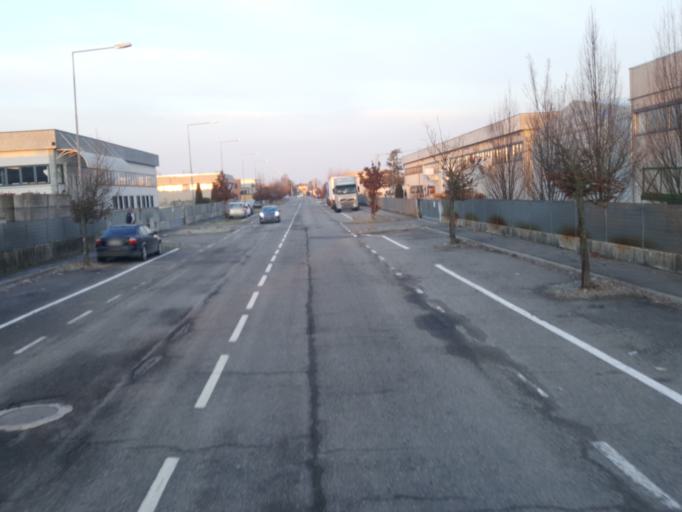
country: IT
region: Emilia-Romagna
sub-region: Provincia di Parma
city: Sorbolo
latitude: 44.8531
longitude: 10.4509
